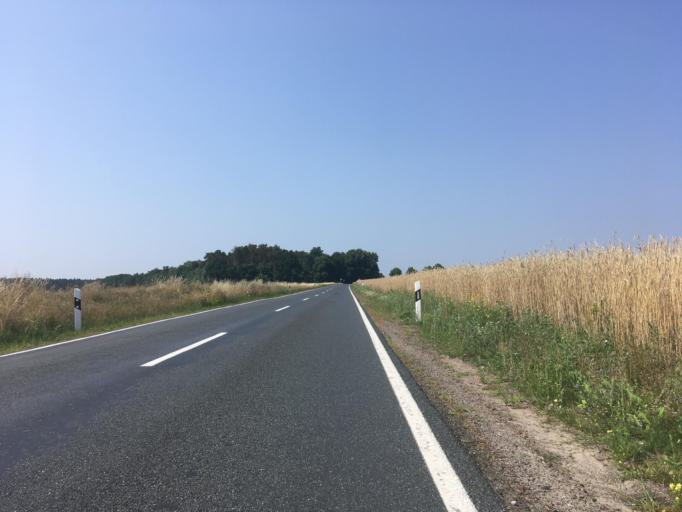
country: DE
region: Brandenburg
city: Golzow
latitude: 52.3017
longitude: 12.6897
